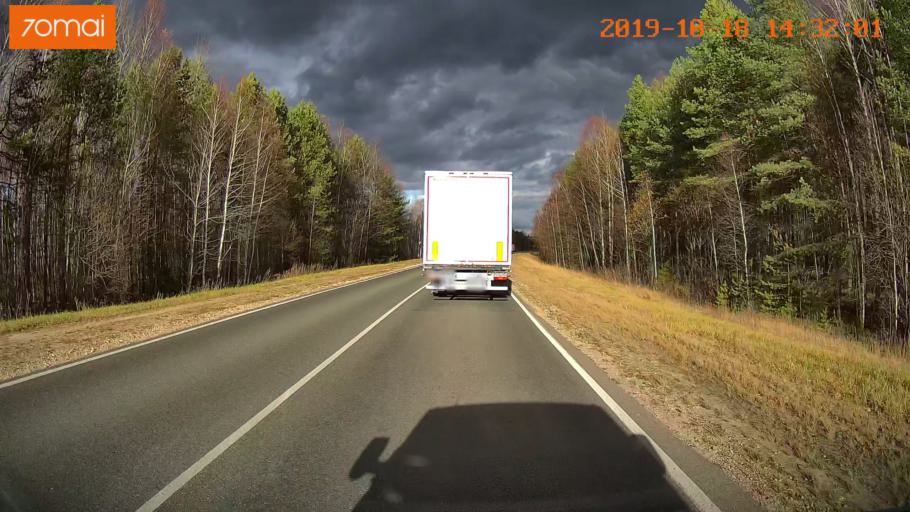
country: RU
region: Rjazan
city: Tuma
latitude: 55.1878
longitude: 40.5742
